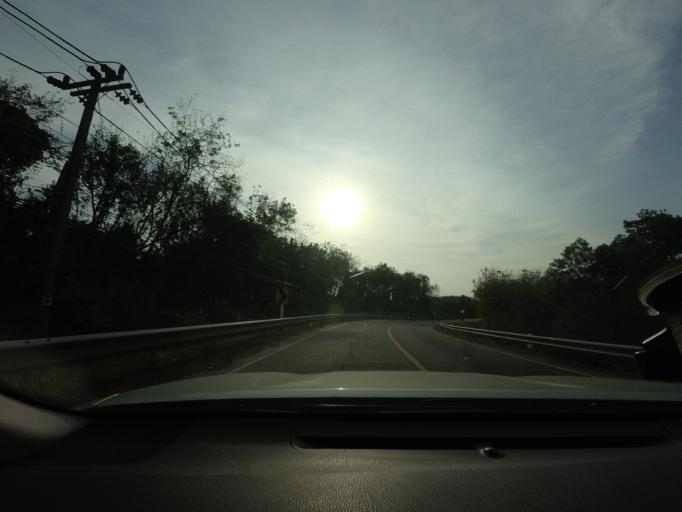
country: TH
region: Narathiwat
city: Ra-ngae
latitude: 6.3376
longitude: 101.7141
